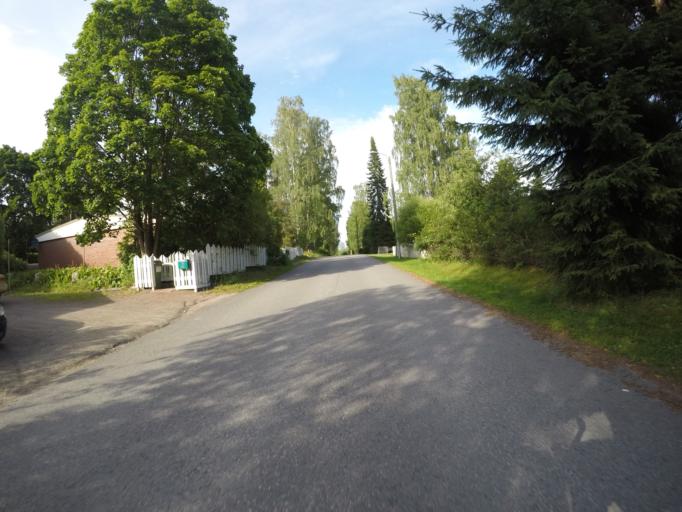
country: FI
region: Haeme
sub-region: Haemeenlinna
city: Haemeenlinna
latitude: 60.9795
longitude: 24.4171
